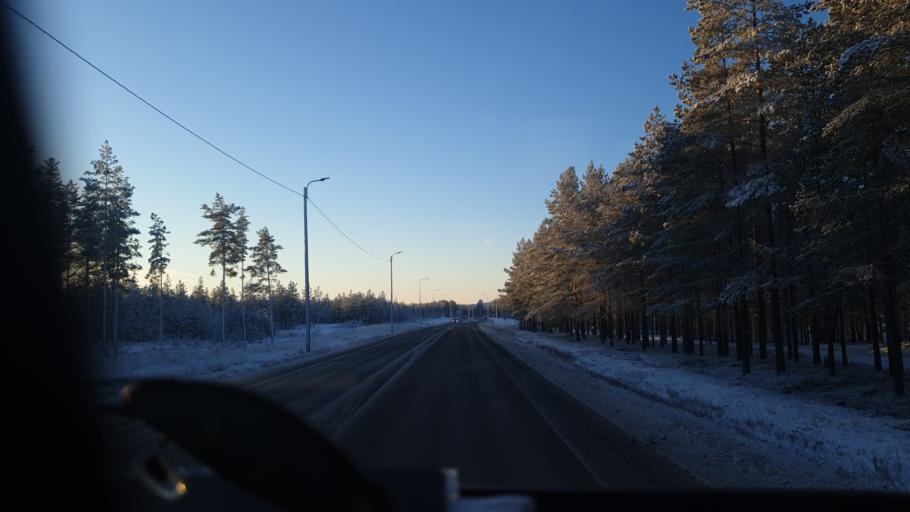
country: FI
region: Northern Ostrobothnia
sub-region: Ylivieska
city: Kalajoki
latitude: 64.2330
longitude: 23.8240
